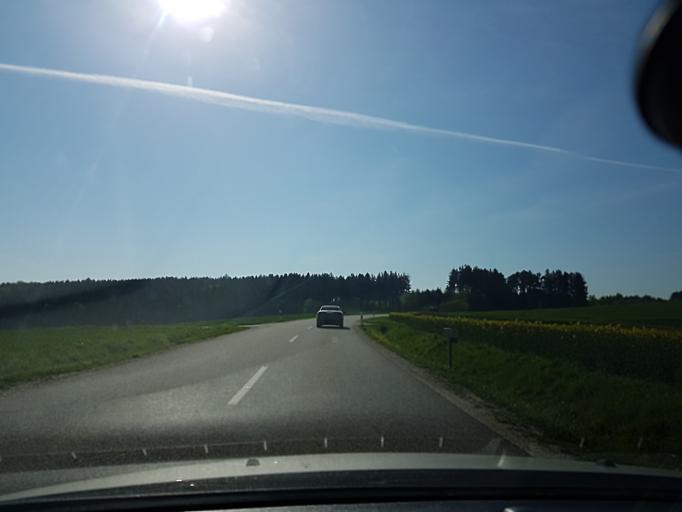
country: DE
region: Bavaria
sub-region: Lower Bavaria
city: Furth
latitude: 48.4012
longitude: 12.3986
